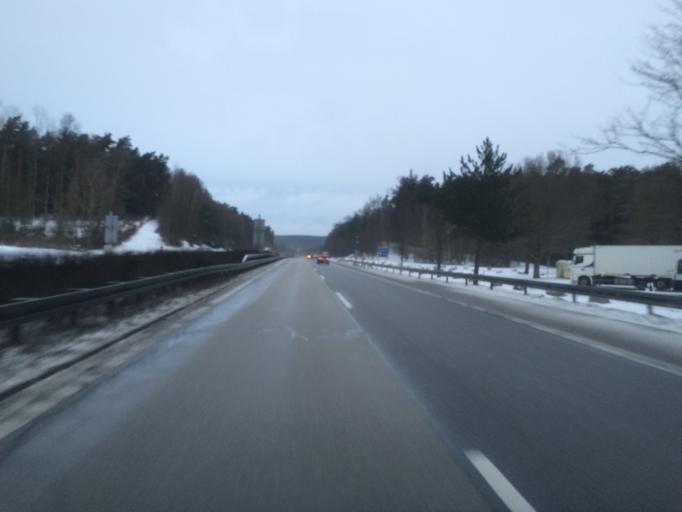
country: DE
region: Bavaria
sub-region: Upper Palatinate
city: Zeitlarn
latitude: 49.0884
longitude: 12.0977
